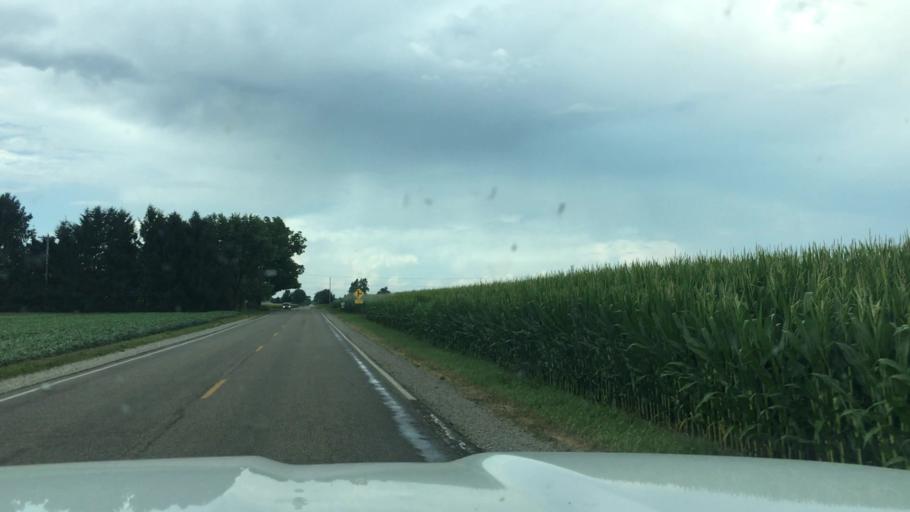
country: US
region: Michigan
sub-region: Montcalm County
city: Carson City
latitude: 43.2028
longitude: -84.7779
